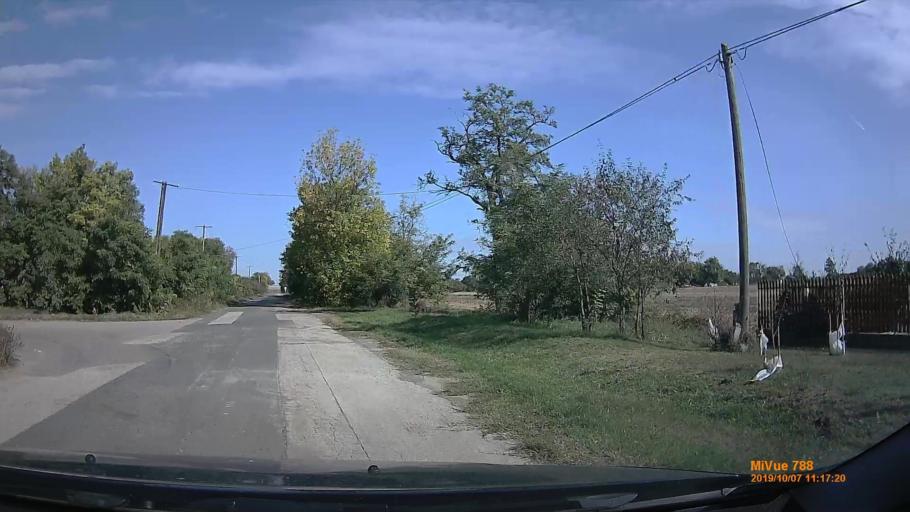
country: HU
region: Bekes
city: Kondoros
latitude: 46.7351
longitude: 20.7829
